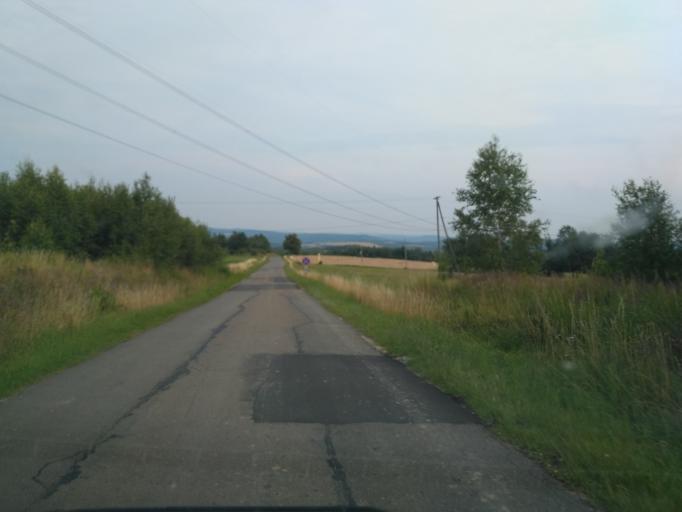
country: PL
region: Subcarpathian Voivodeship
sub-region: Powiat strzyzowski
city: Jawornik
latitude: 49.8684
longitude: 21.8615
